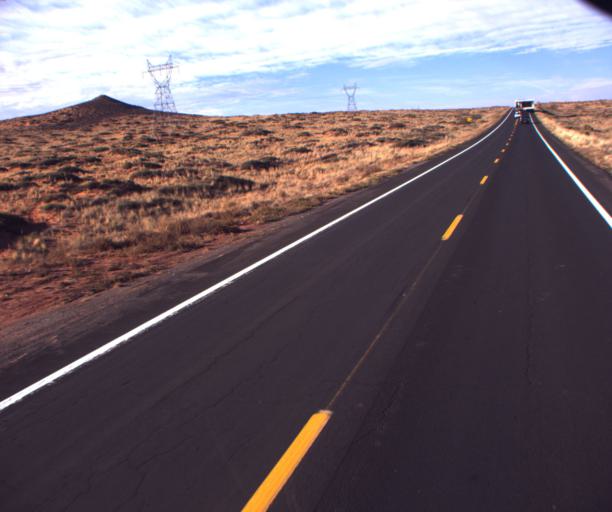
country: US
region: Arizona
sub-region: Apache County
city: Lukachukai
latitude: 36.9544
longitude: -109.5073
